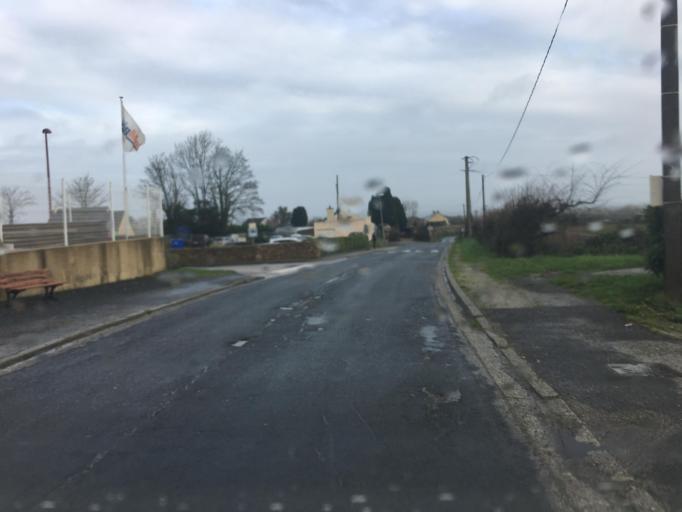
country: FR
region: Lower Normandy
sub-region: Departement de la Manche
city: Saint-Pierre-Eglise
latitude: 49.6713
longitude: -1.4043
